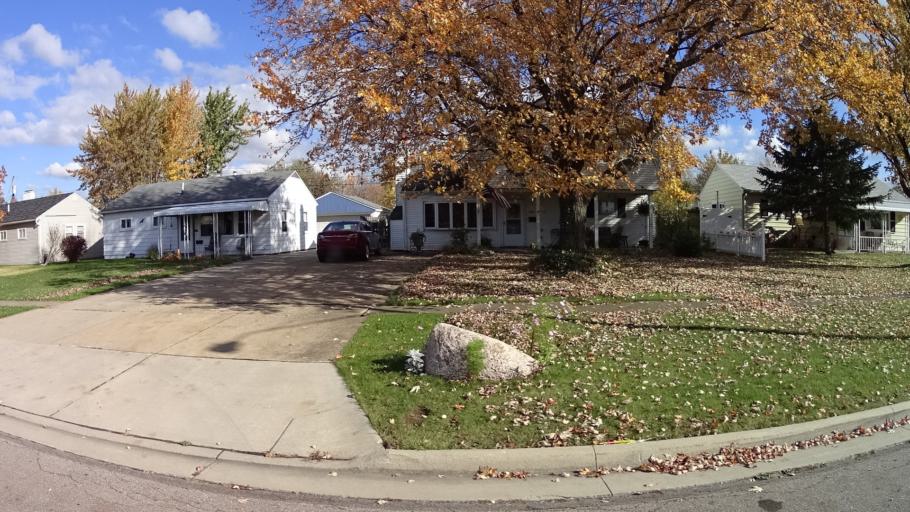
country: US
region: Ohio
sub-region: Lorain County
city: Sheffield
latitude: 41.4288
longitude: -82.1096
